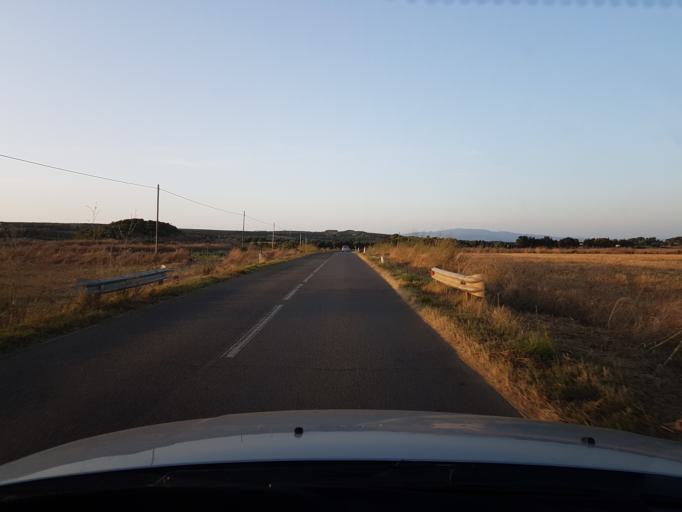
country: IT
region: Sardinia
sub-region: Provincia di Oristano
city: Cabras
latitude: 39.9085
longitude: 8.4387
